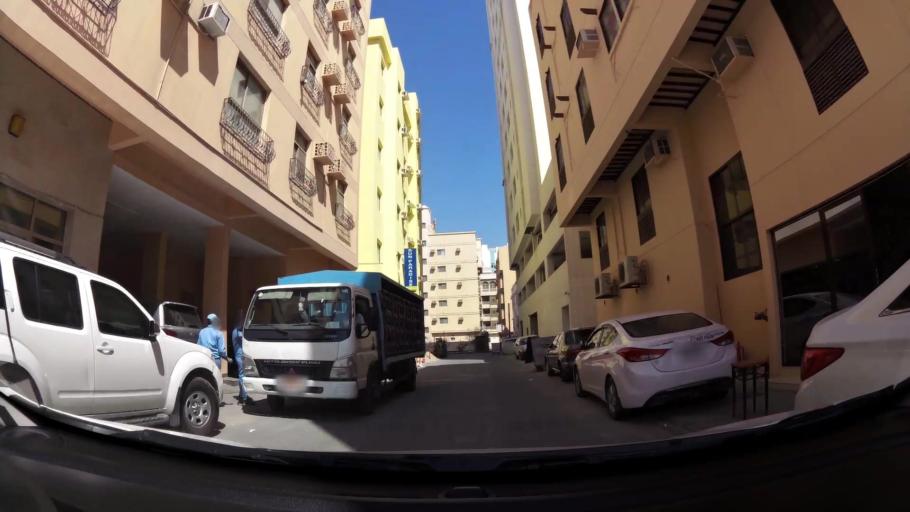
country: BH
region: Manama
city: Manama
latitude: 26.2131
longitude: 50.6041
